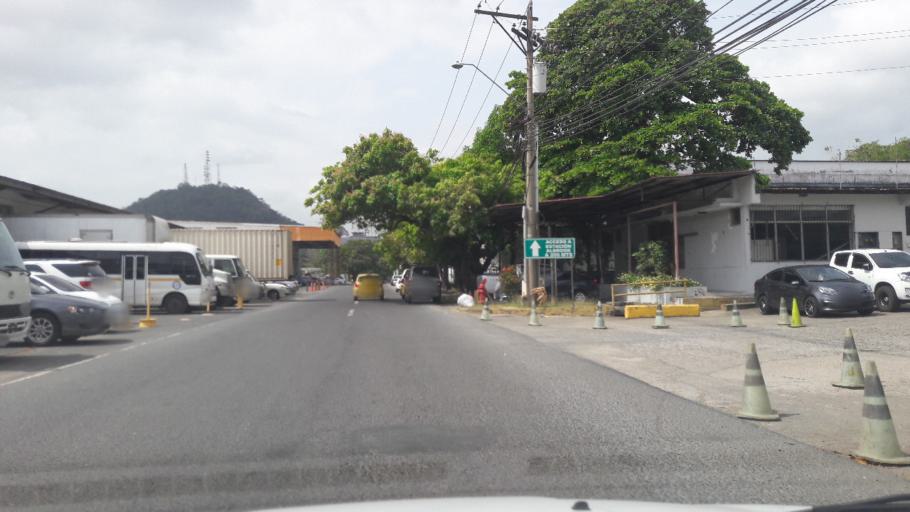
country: PA
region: Panama
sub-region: Distrito de Panama
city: Ancon
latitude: 8.9730
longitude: -79.5474
